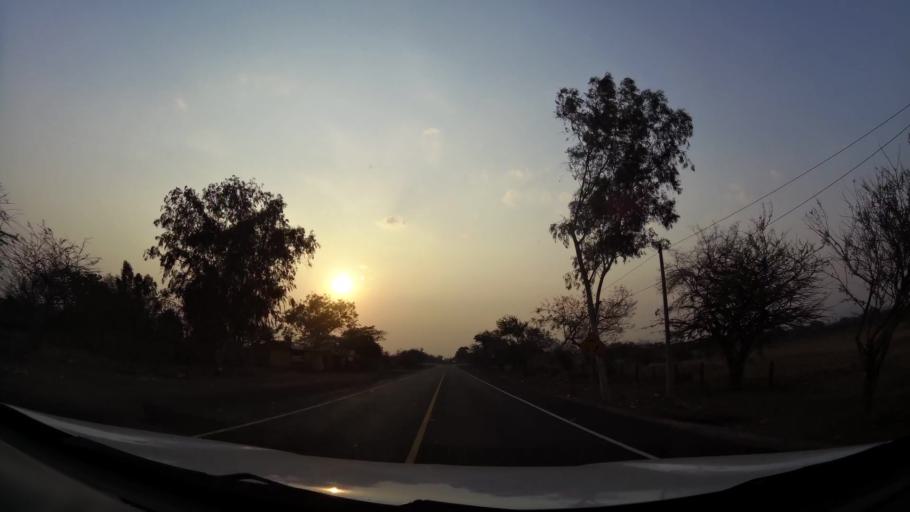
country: NI
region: Leon
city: La Paz Centro
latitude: 12.3346
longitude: -86.6532
